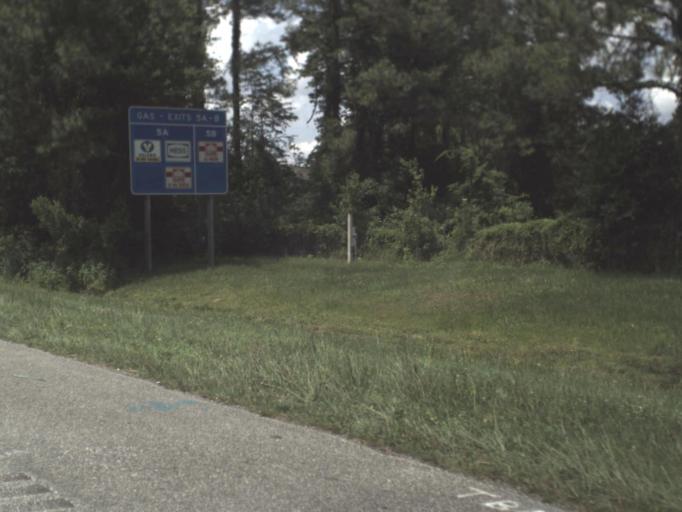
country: US
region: Florida
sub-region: Saint Johns County
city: Fruit Cove
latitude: 30.1763
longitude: -81.6204
